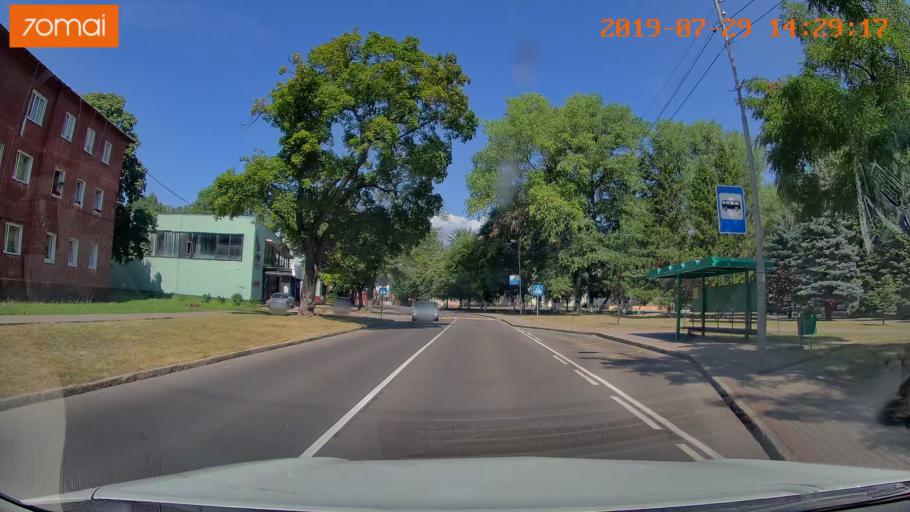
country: RU
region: Kaliningrad
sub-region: Gorod Kaliningrad
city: Baltiysk
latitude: 54.6426
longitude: 19.8916
